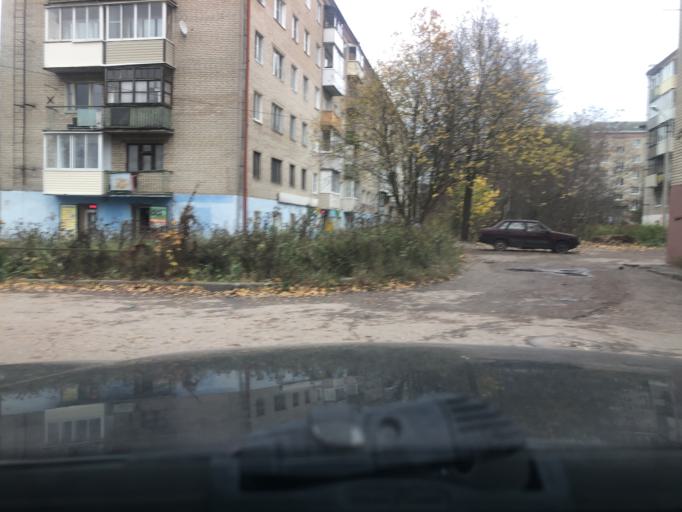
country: RU
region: Moskovskaya
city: Sergiyev Posad
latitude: 56.2964
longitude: 38.1168
